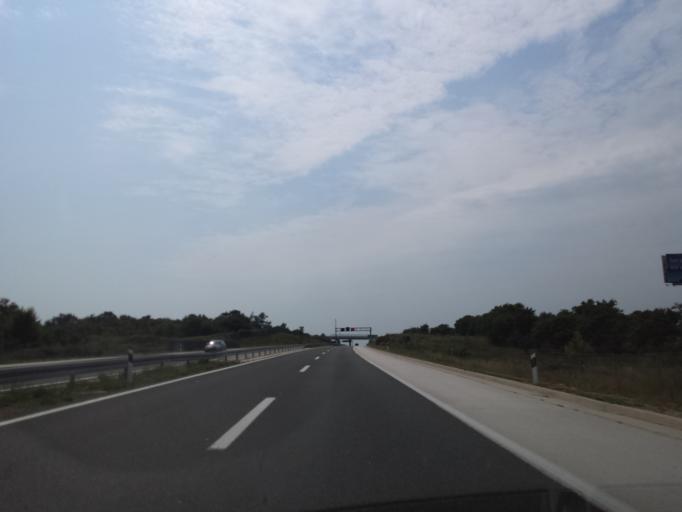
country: HR
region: Zadarska
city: Posedarje
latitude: 44.1959
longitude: 15.4398
